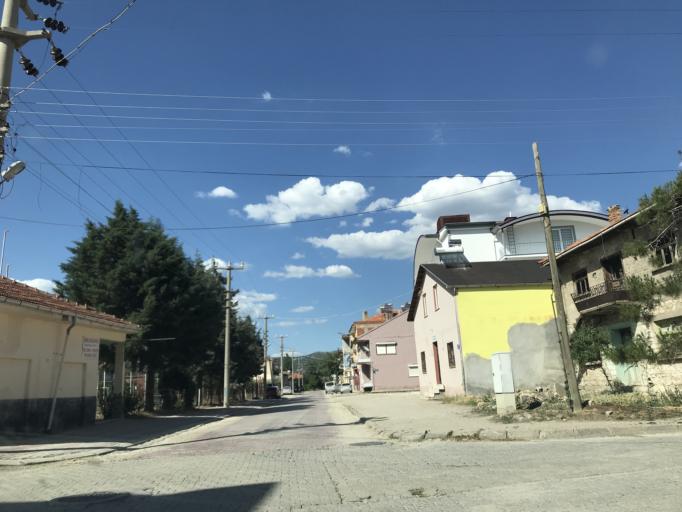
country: TR
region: Denizli
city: Civril
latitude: 38.3028
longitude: 29.7445
